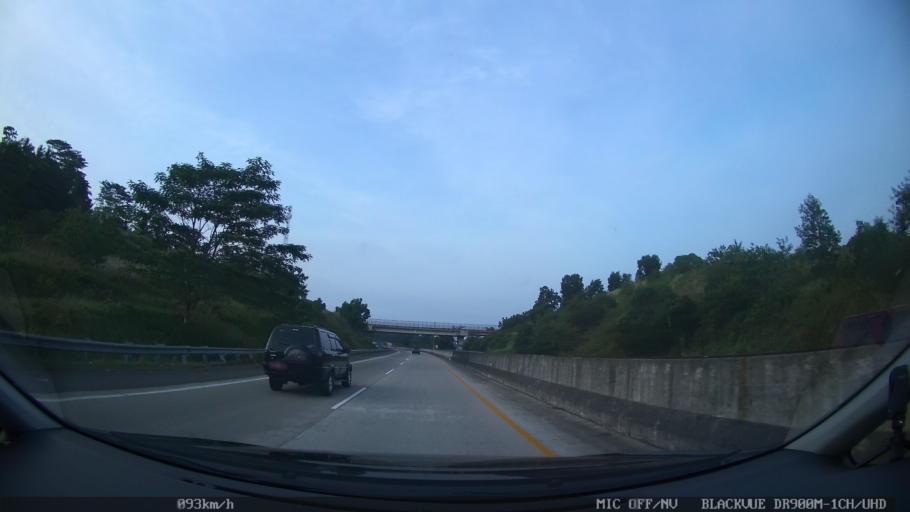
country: ID
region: Lampung
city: Penengahan
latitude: -5.8221
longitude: 105.7352
